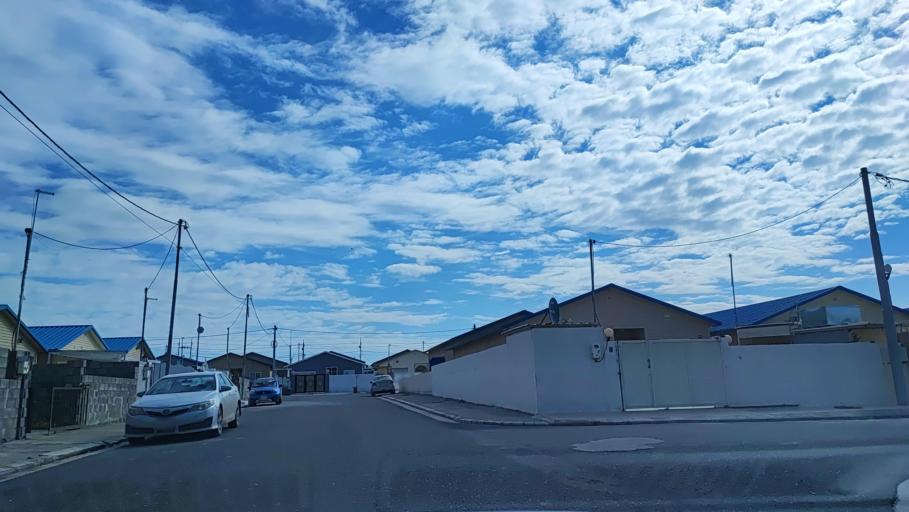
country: IQ
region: Arbil
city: Erbil
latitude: 36.2864
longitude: 44.0770
